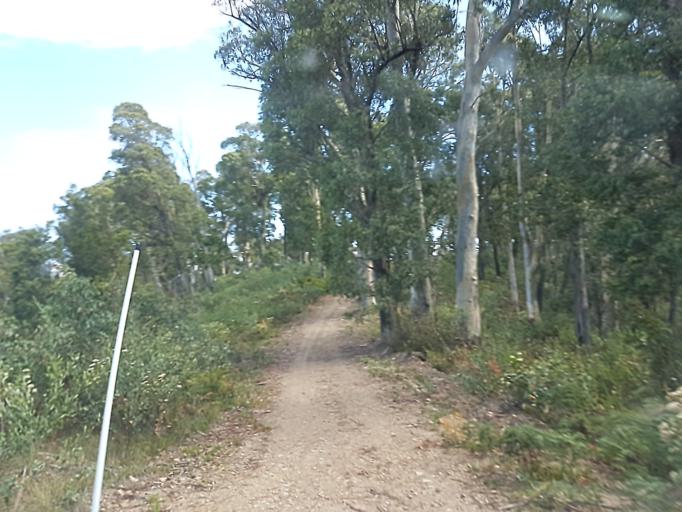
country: AU
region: Victoria
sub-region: Alpine
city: Mount Beauty
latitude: -36.9180
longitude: 146.9983
